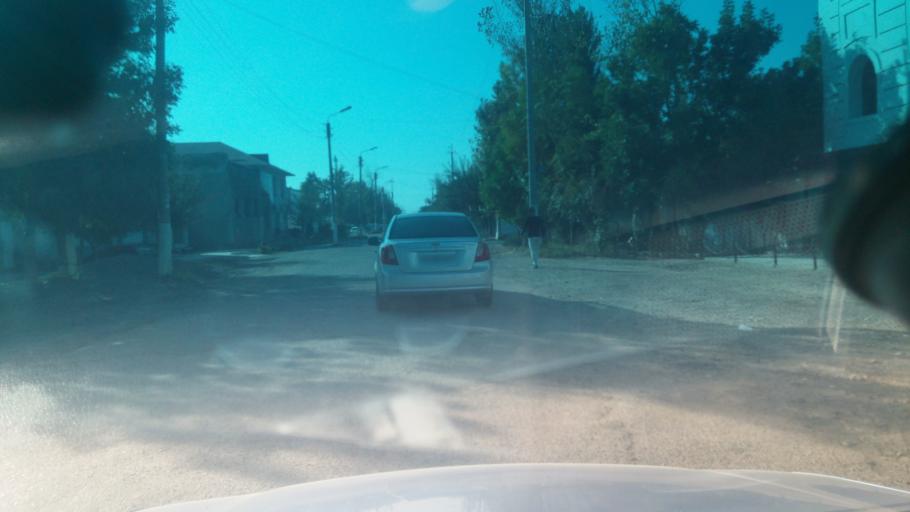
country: UZ
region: Sirdaryo
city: Guliston
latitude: 40.4976
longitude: 68.7688
